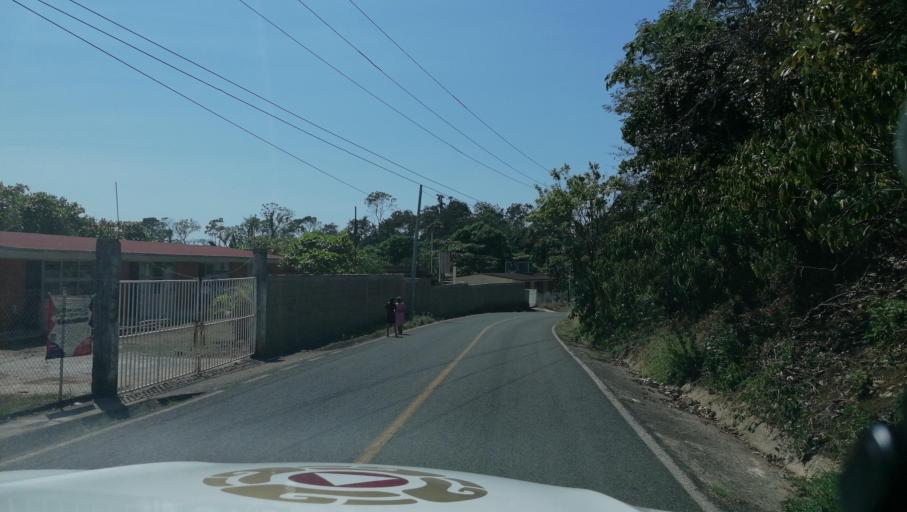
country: MX
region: Chiapas
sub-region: Cacahoatan
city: Benito Juarez
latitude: 15.0199
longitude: -92.2226
